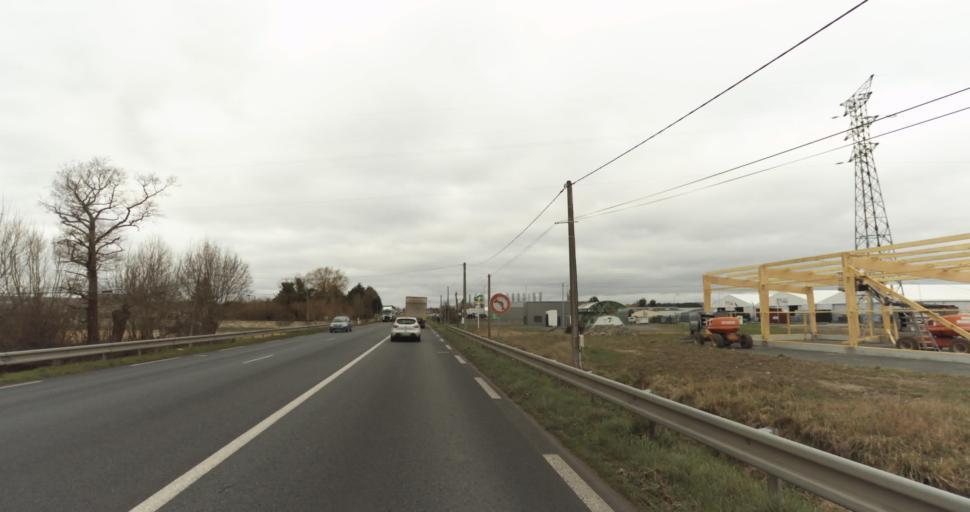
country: FR
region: Pays de la Loire
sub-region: Departement de Maine-et-Loire
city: Vivy
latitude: 47.3651
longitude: -0.0934
